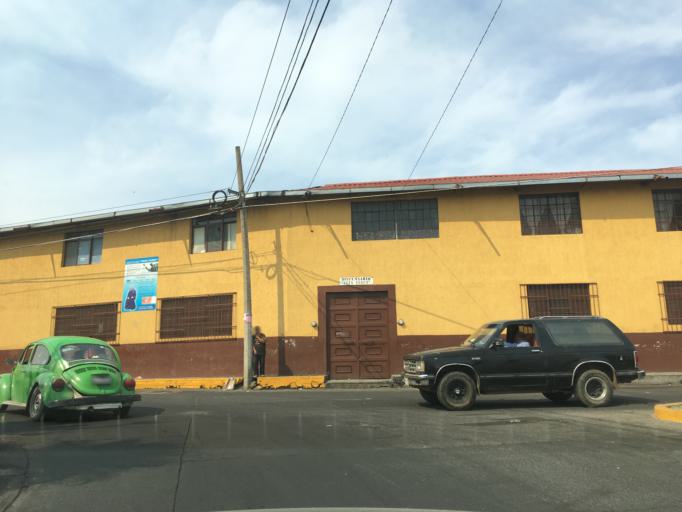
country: MX
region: Michoacan
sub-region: Uruapan
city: Uruapan
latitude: 19.4052
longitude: -102.0664
